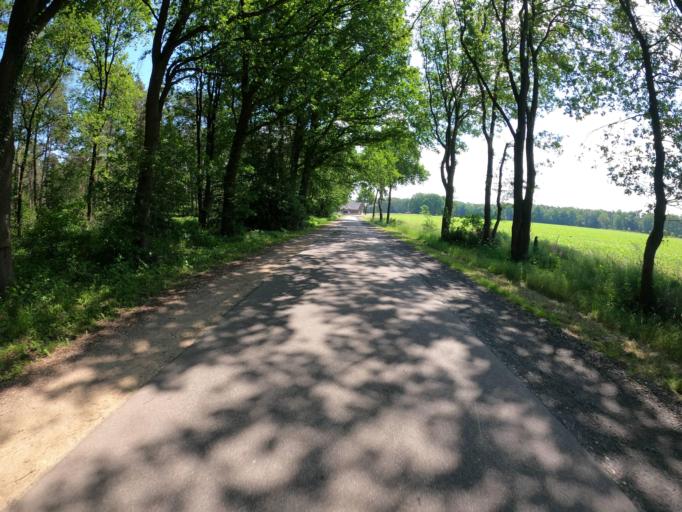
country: DE
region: North Rhine-Westphalia
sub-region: Regierungsbezirk Dusseldorf
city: Hunxe
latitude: 51.7058
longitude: 6.7852
